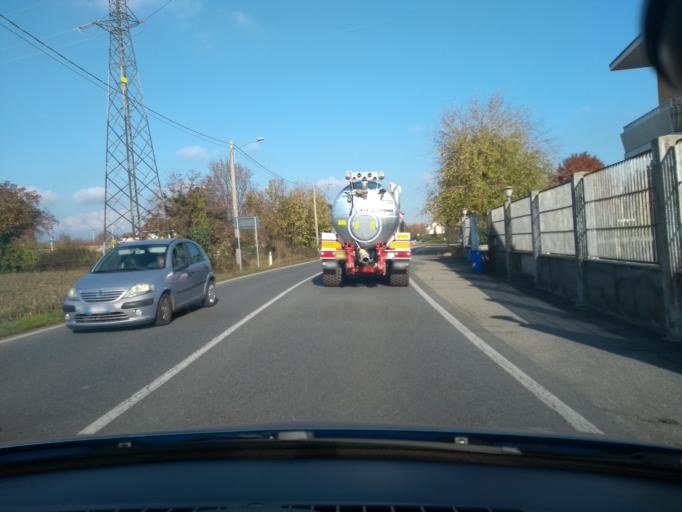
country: IT
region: Piedmont
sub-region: Provincia di Torino
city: Cirie
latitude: 45.2204
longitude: 7.5978
